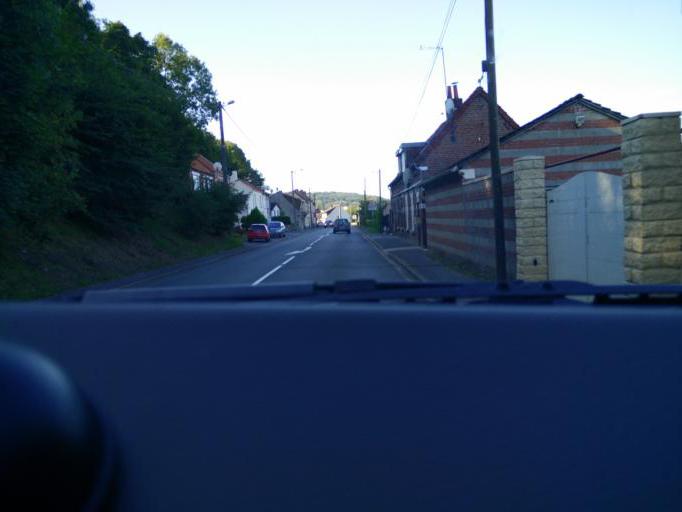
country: FR
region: Nord-Pas-de-Calais
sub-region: Departement du Pas-de-Calais
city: Divion
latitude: 50.4593
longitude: 2.4831
